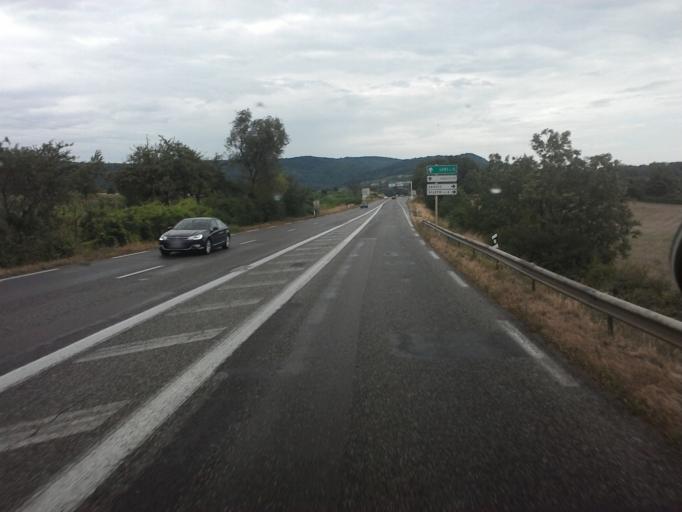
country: FR
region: Franche-Comte
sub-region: Departement du Jura
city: Arbois
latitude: 46.9192
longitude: 5.7723
